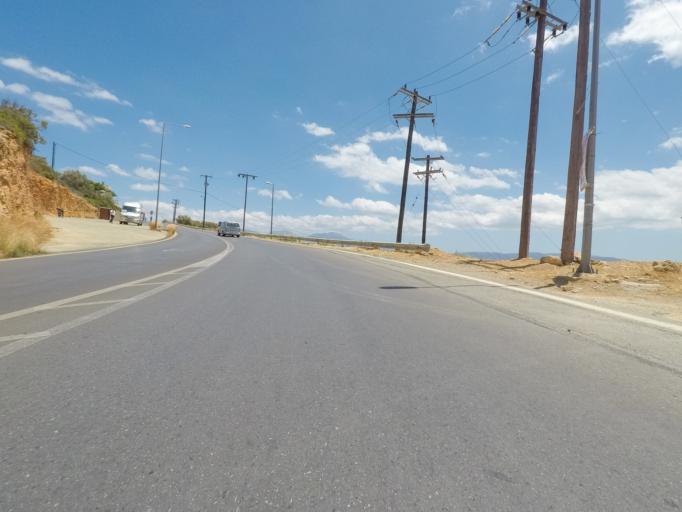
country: GR
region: Crete
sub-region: Nomos Lasithiou
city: Agios Nikolaos
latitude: 35.2201
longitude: 25.7098
